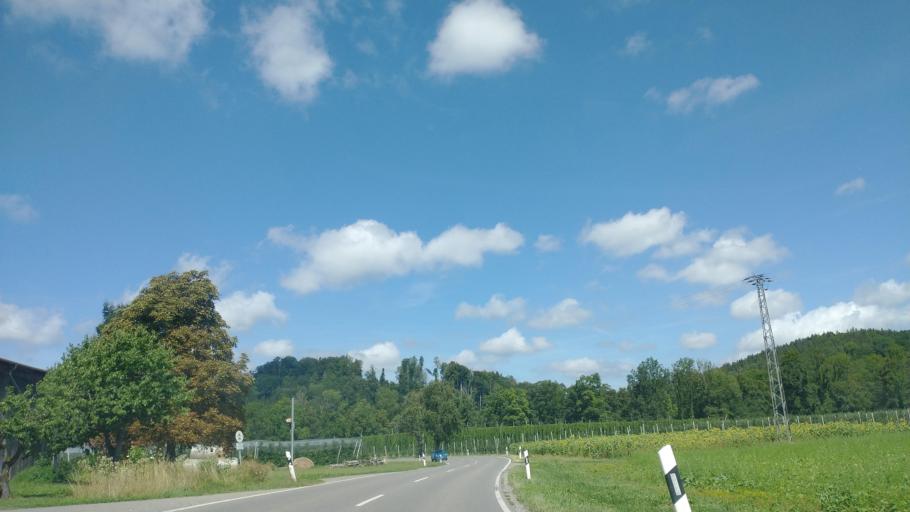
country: DE
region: Baden-Wuerttemberg
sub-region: Tuebingen Region
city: Kressbronn am Bodensee
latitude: 47.6276
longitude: 9.6019
